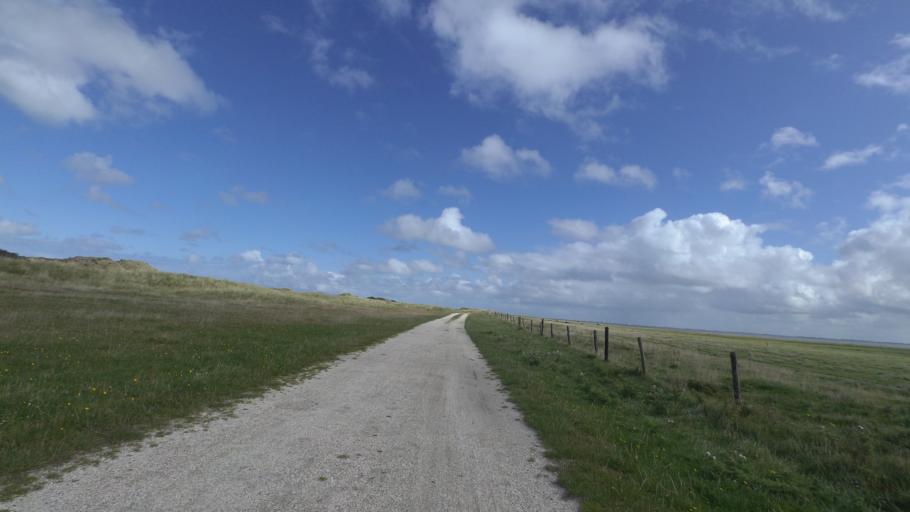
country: NL
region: Friesland
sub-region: Gemeente Ameland
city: Nes
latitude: 53.4473
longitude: 5.8541
